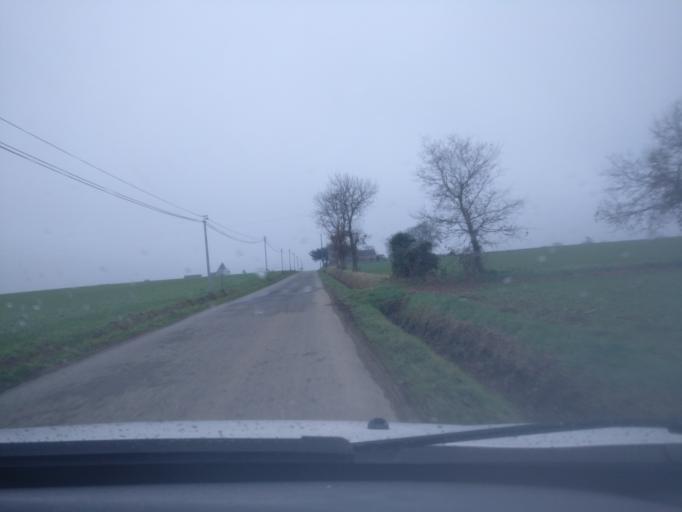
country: FR
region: Brittany
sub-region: Departement d'Ille-et-Vilaine
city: Chasne-sur-Illet
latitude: 48.2943
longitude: -1.5987
